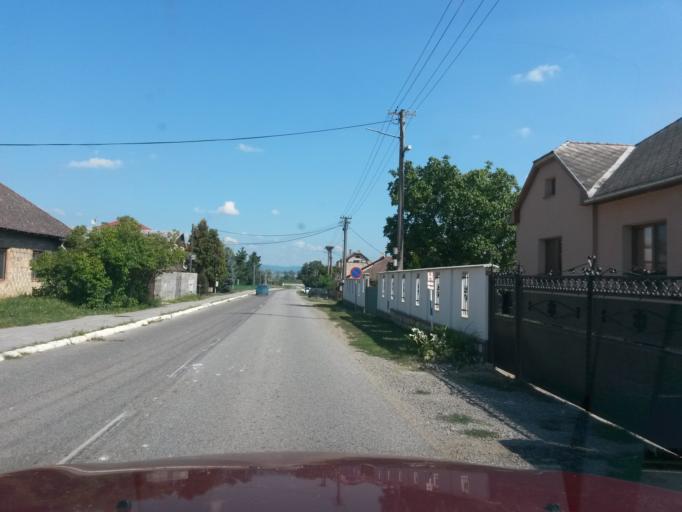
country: SK
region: Kosicky
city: Moldava nad Bodvou
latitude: 48.5351
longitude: 21.0777
